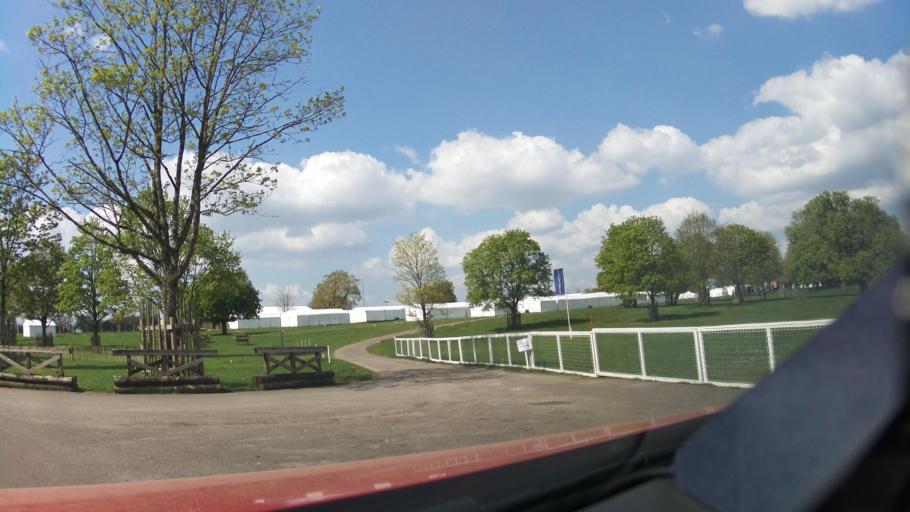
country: GB
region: England
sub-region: Wiltshire
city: Luckington
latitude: 51.5459
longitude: -2.2826
